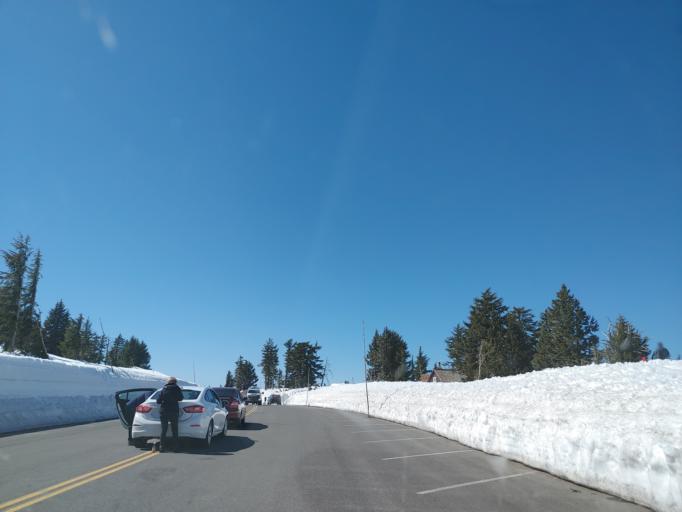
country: US
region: Oregon
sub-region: Jackson County
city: Shady Cove
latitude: 42.9104
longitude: -122.1427
